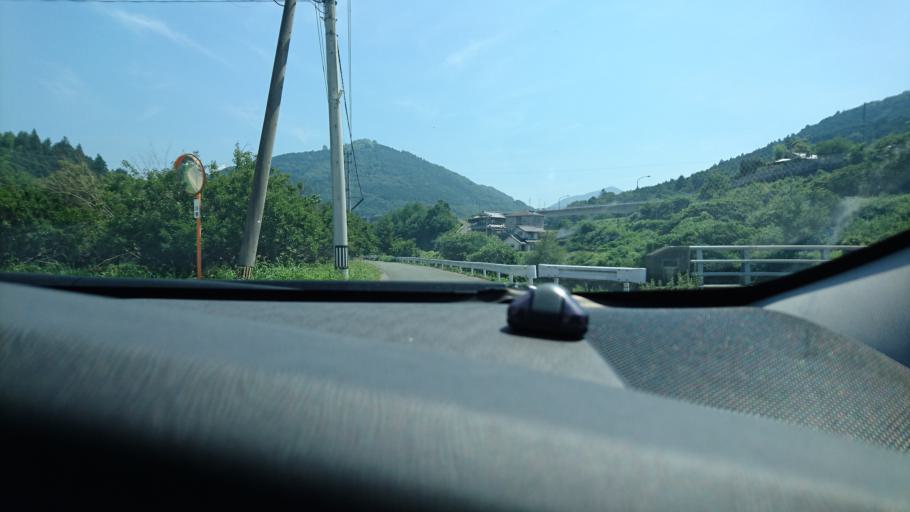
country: JP
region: Ehime
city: Ozu
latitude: 33.4984
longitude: 132.5493
